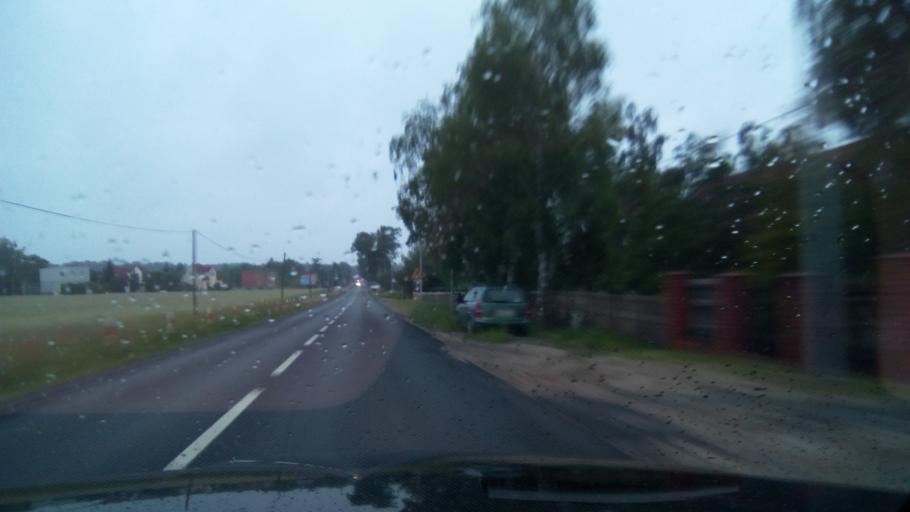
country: PL
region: Greater Poland Voivodeship
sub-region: Powiat poznanski
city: Kobylnica
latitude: 52.4373
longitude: 17.0742
